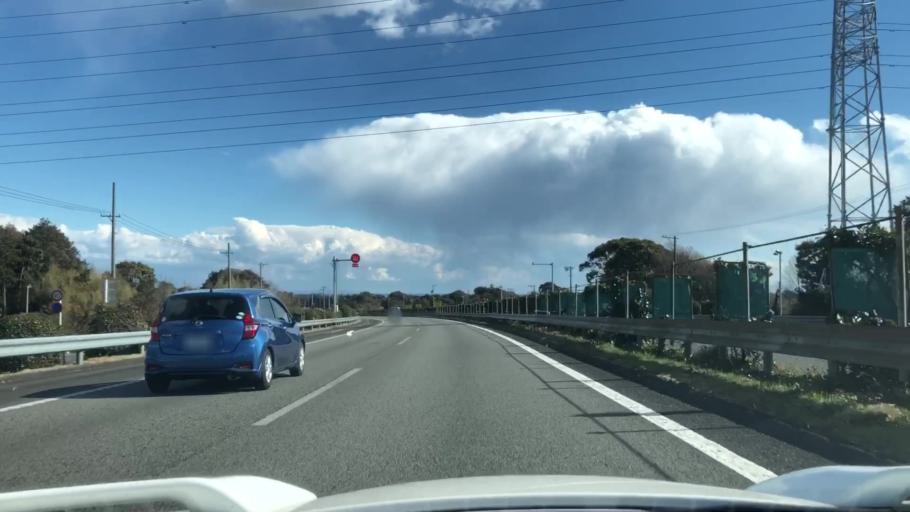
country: JP
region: Shizuoka
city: Shimada
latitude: 34.7564
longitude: 138.1718
